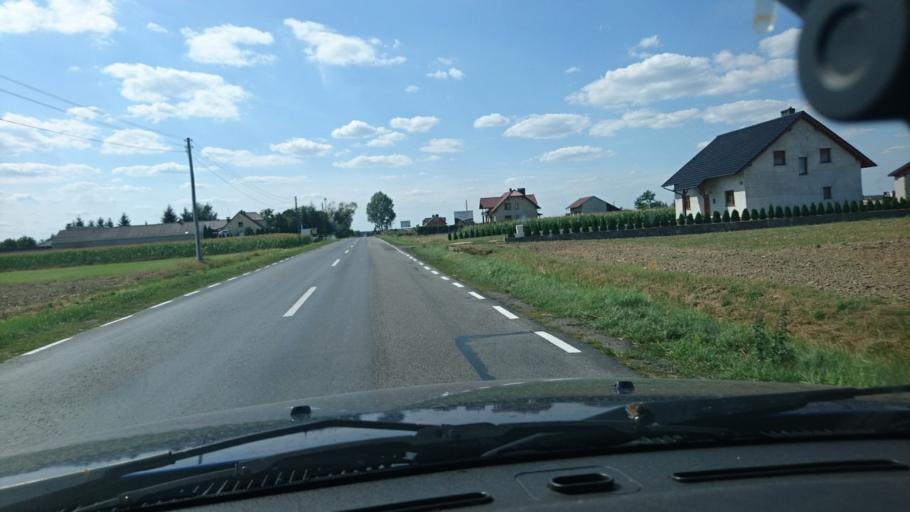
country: PL
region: Greater Poland Voivodeship
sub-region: Powiat krotoszynski
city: Sulmierzyce
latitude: 51.6052
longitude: 17.5534
